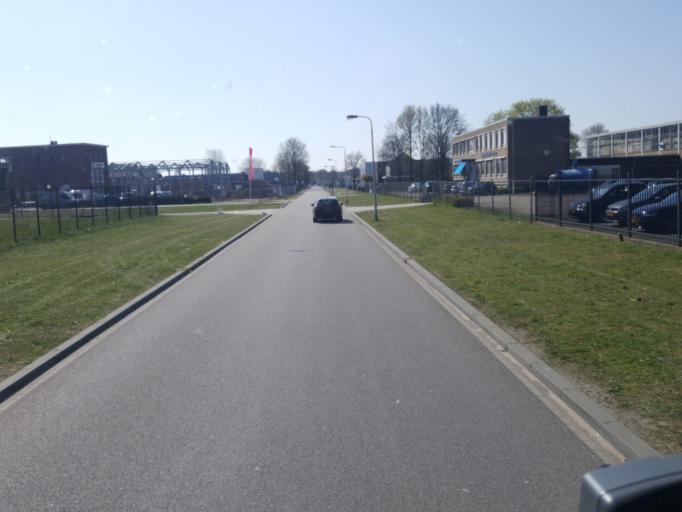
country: NL
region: North Brabant
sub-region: Gemeente Oss
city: Berghem
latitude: 51.7649
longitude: 5.5499
